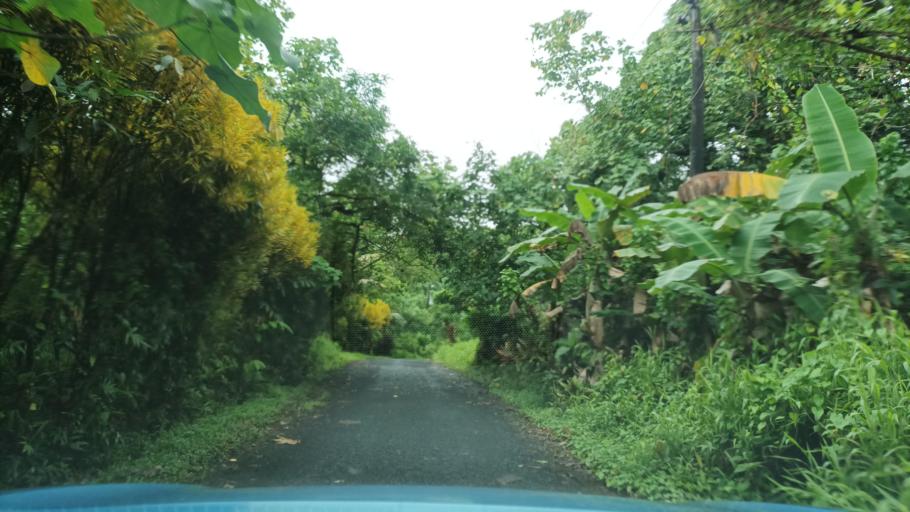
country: FM
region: Pohnpei
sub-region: Kolonia Municipality
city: Kolonia
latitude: 6.9211
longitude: 158.2774
